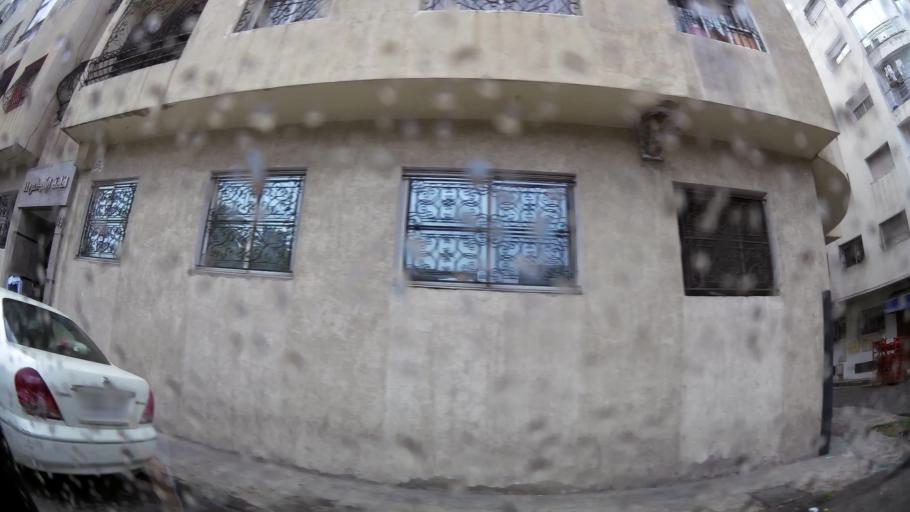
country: MA
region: Grand Casablanca
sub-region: Casablanca
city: Casablanca
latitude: 33.5810
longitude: -7.5983
